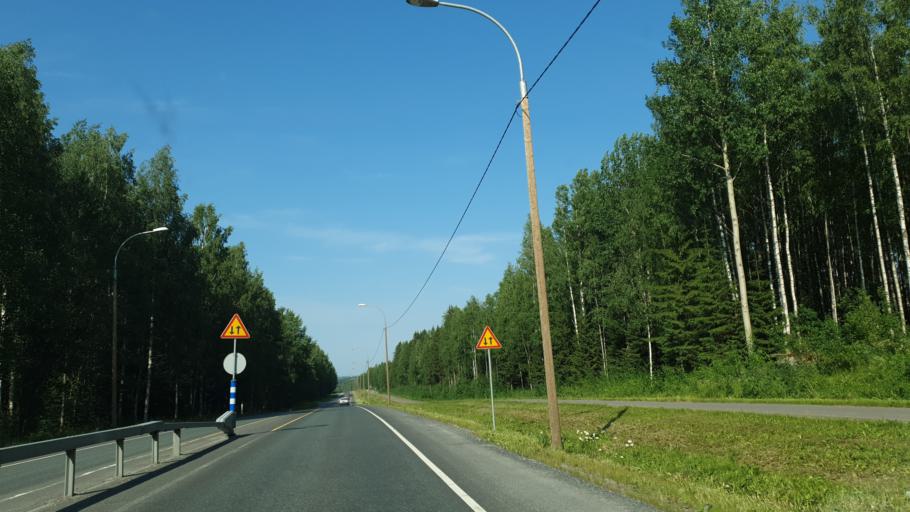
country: FI
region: Northern Savo
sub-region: Kuopio
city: Siilinjaervi
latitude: 63.1035
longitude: 27.7440
